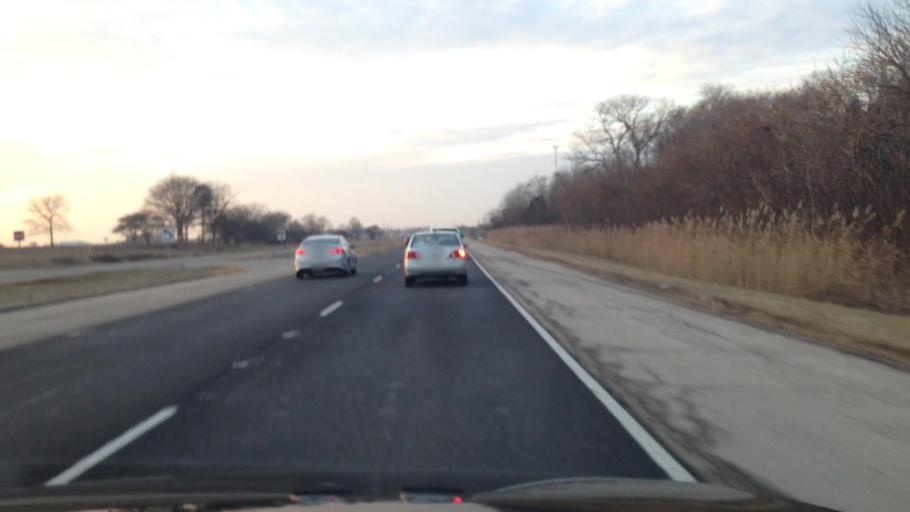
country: US
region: Illinois
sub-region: Cook County
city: Streamwood
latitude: 42.0696
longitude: -88.1717
